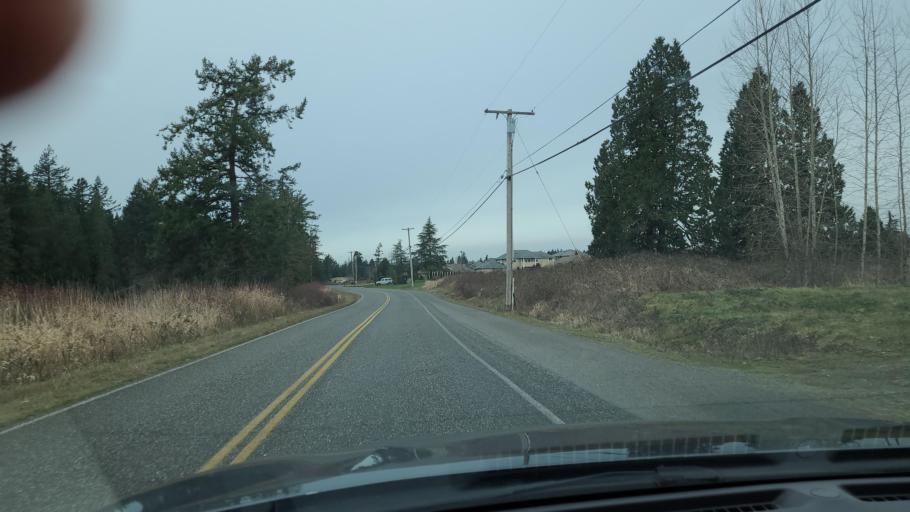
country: US
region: Washington
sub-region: Whatcom County
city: Birch Bay
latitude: 48.9515
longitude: -122.7147
